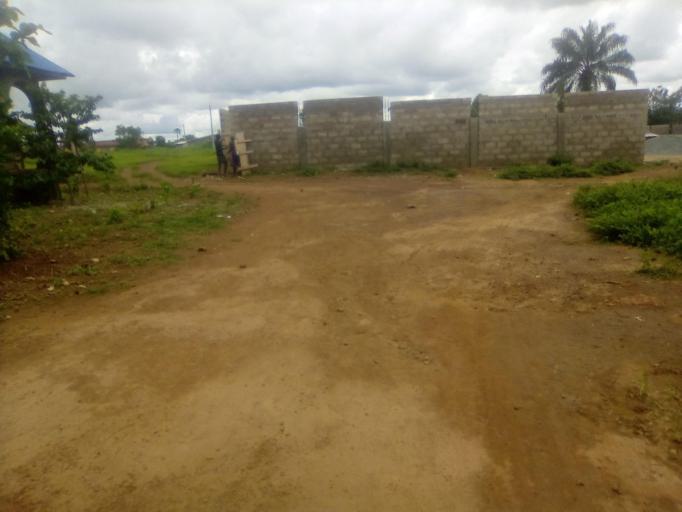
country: SL
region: Southern Province
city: Moyamba
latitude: 8.1485
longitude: -12.4344
